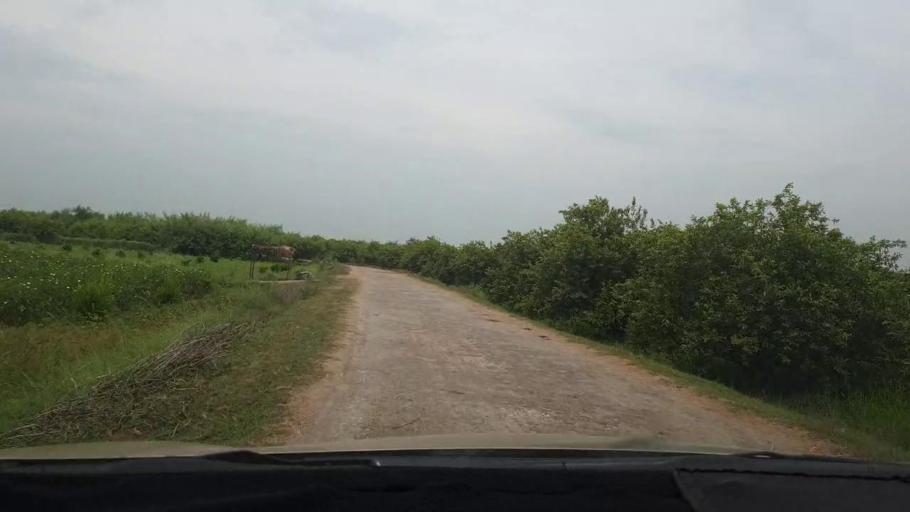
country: PK
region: Sindh
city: Naudero
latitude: 27.6343
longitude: 68.3430
